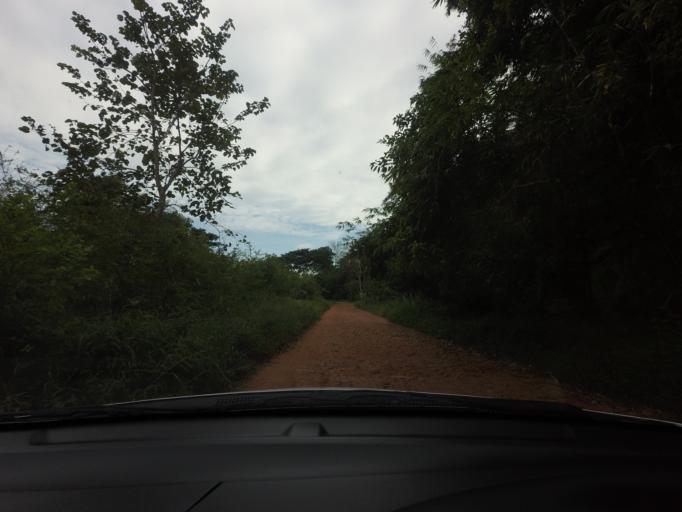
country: TH
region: Nakhon Nayok
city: Nakhon Nayok
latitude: 14.3406
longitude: 101.2809
